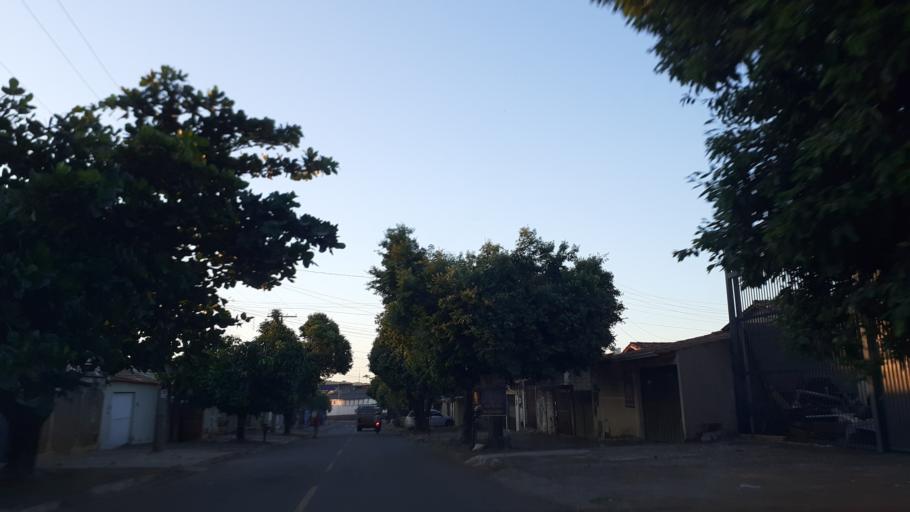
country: BR
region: Goias
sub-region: Goiania
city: Goiania
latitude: -16.7018
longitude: -49.3286
